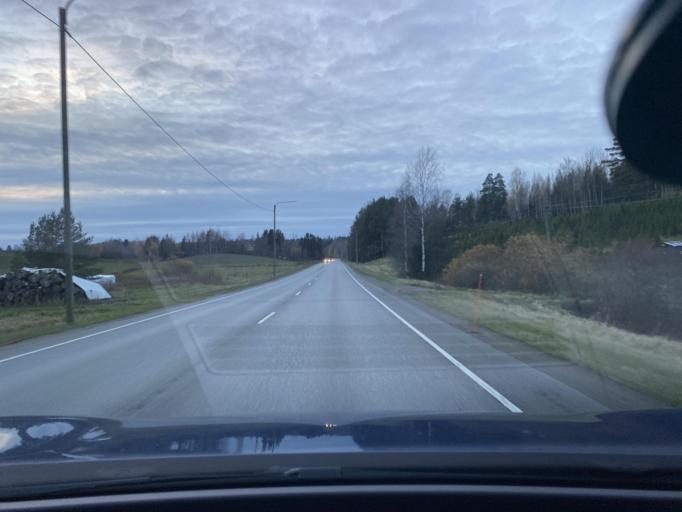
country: FI
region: Uusimaa
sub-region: Helsinki
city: Saukkola
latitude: 60.3886
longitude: 24.0427
